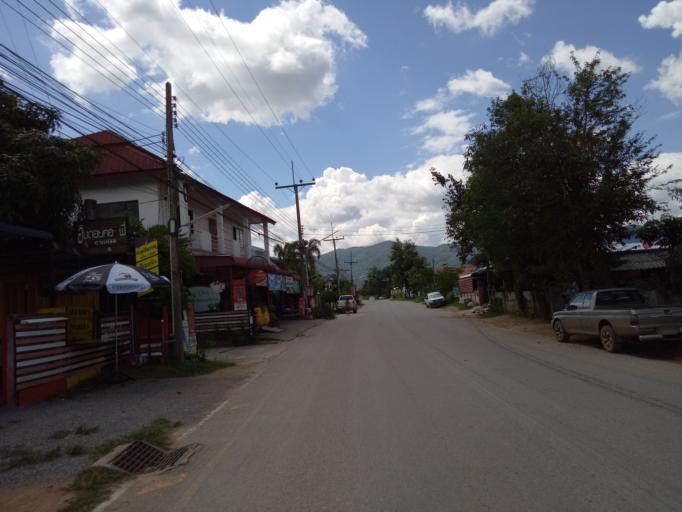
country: TH
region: Chiang Rai
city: Chiang Rai
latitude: 19.9964
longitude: 99.8265
